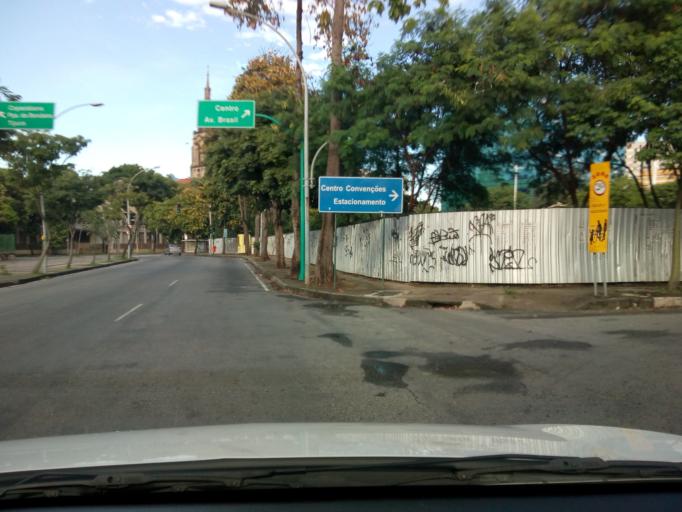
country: BR
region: Rio de Janeiro
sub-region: Rio De Janeiro
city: Rio de Janeiro
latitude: -22.9131
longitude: -43.2075
